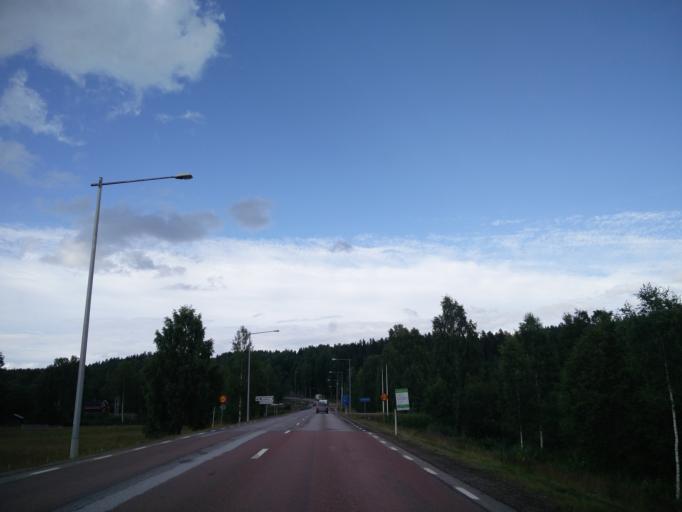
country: SE
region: Vaermland
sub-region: Hagfors Kommun
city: Ekshaerad
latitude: 60.4205
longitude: 13.2544
